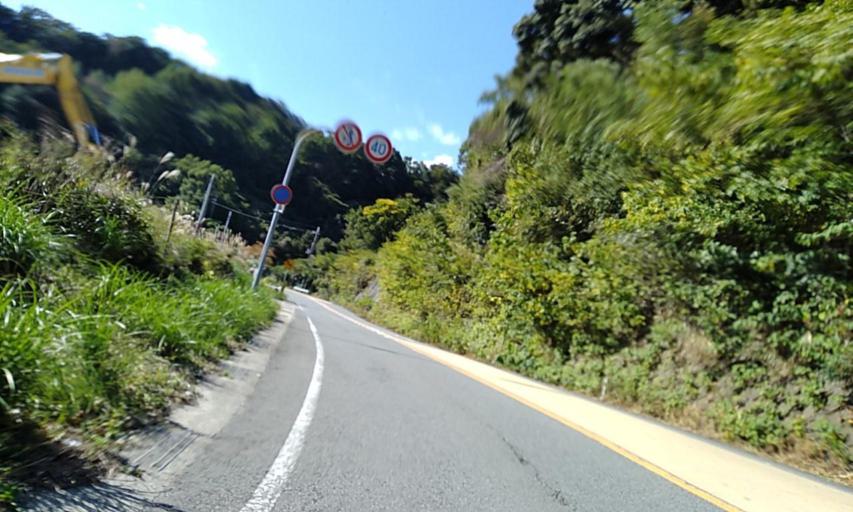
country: JP
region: Wakayama
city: Gobo
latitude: 33.9930
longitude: 135.1887
